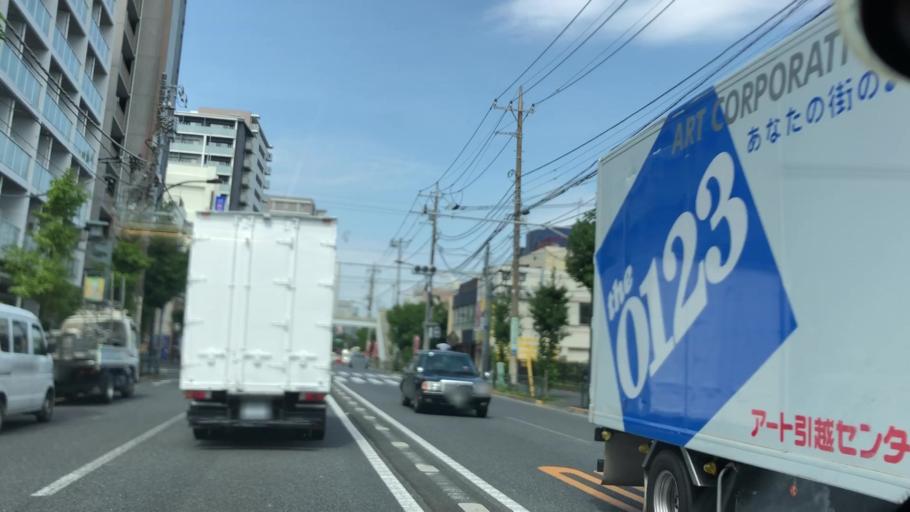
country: JP
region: Tokyo
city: Urayasu
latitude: 35.6894
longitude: 139.8311
